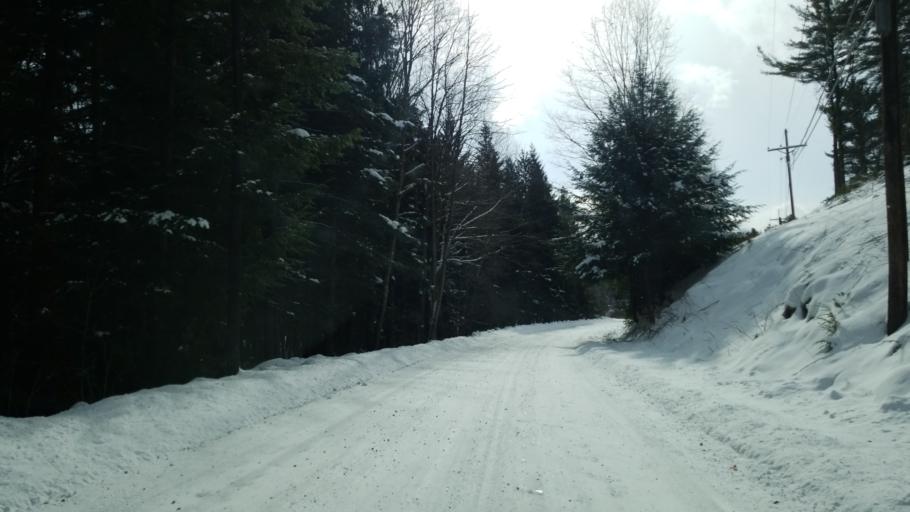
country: US
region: Pennsylvania
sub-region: Clearfield County
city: Clearfield
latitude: 41.0491
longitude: -78.4643
